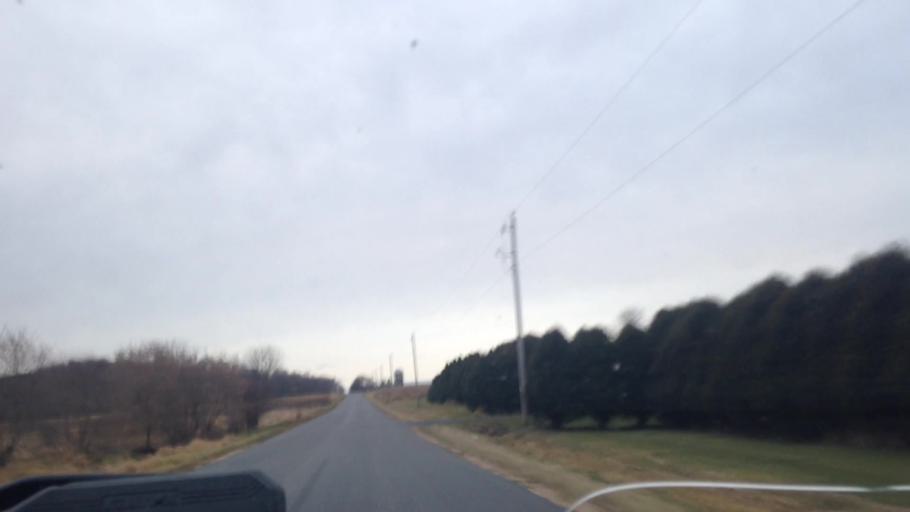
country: US
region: Wisconsin
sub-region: Dodge County
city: Theresa
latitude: 43.4860
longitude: -88.4673
